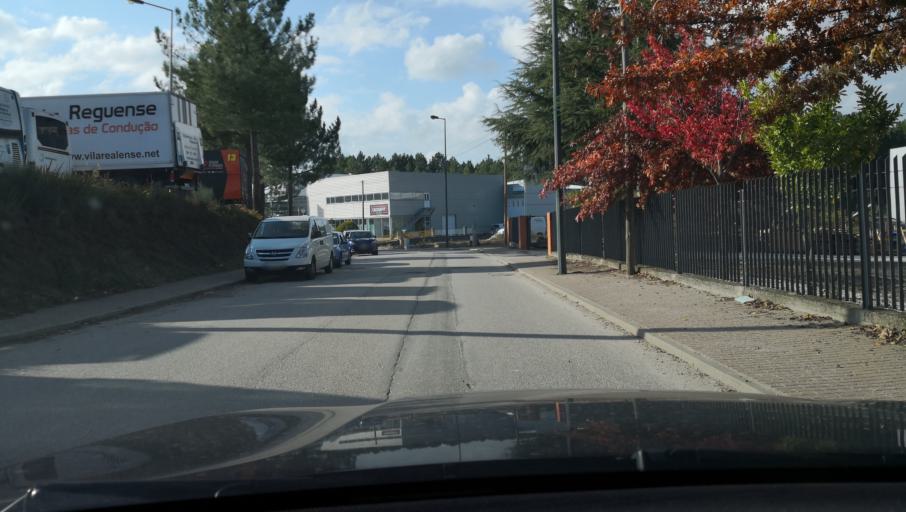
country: PT
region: Vila Real
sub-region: Vila Real
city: Vila Real
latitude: 41.2774
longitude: -7.7142
